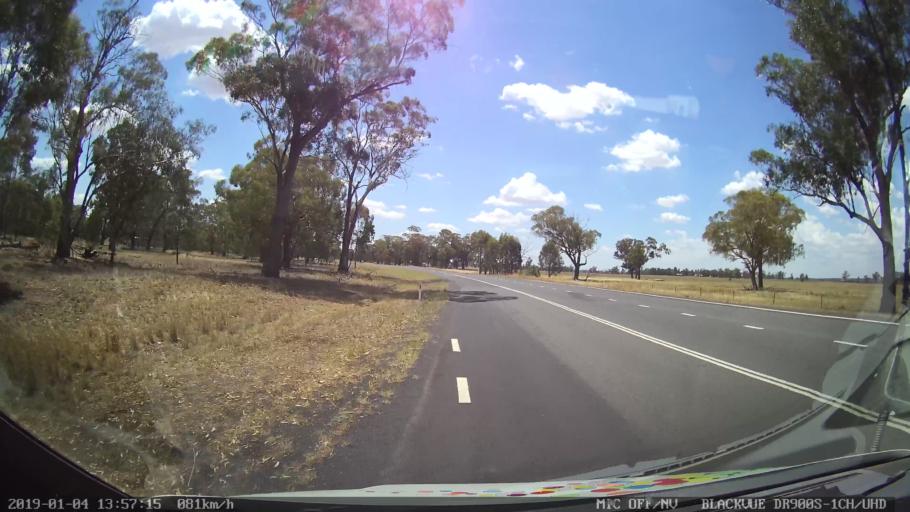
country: AU
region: New South Wales
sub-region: Dubbo Municipality
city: Dubbo
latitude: -32.3422
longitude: 148.6001
